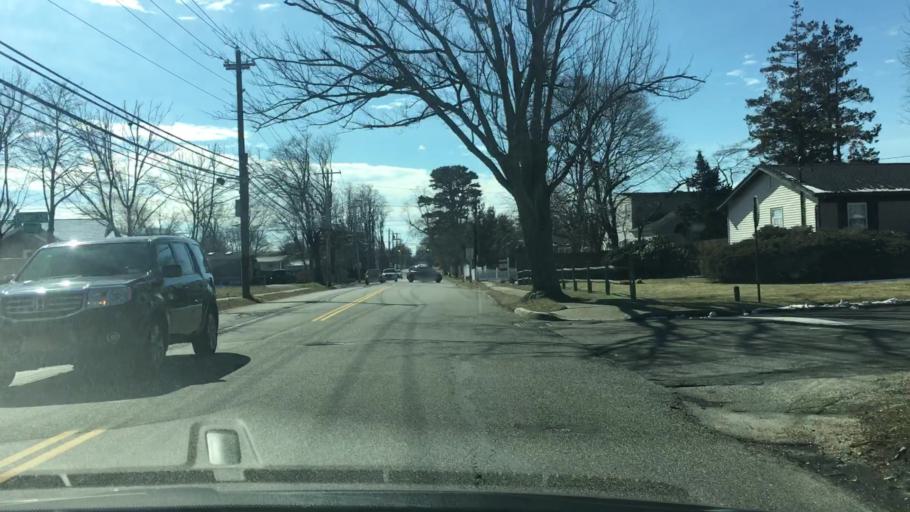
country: US
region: New York
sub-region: Suffolk County
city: West Babylon
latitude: 40.7250
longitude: -73.3464
